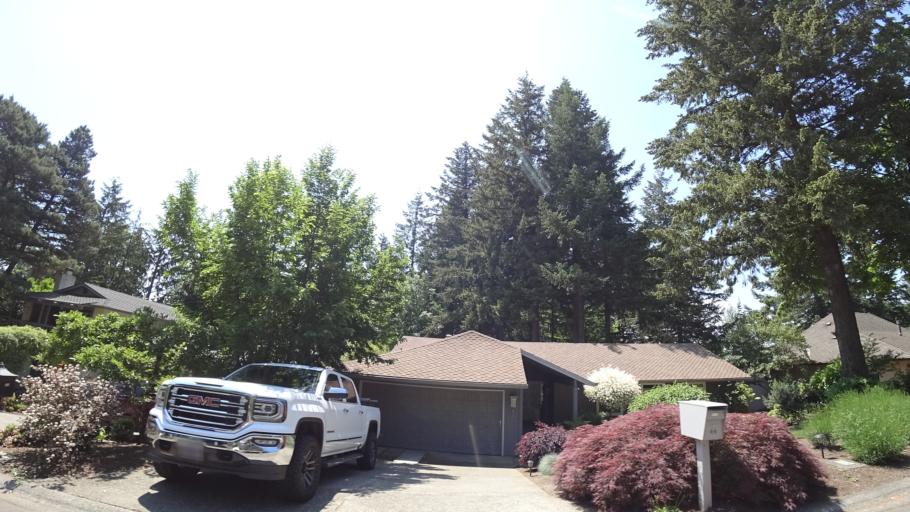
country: US
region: Oregon
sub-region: Washington County
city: Metzger
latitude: 45.4310
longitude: -122.7206
